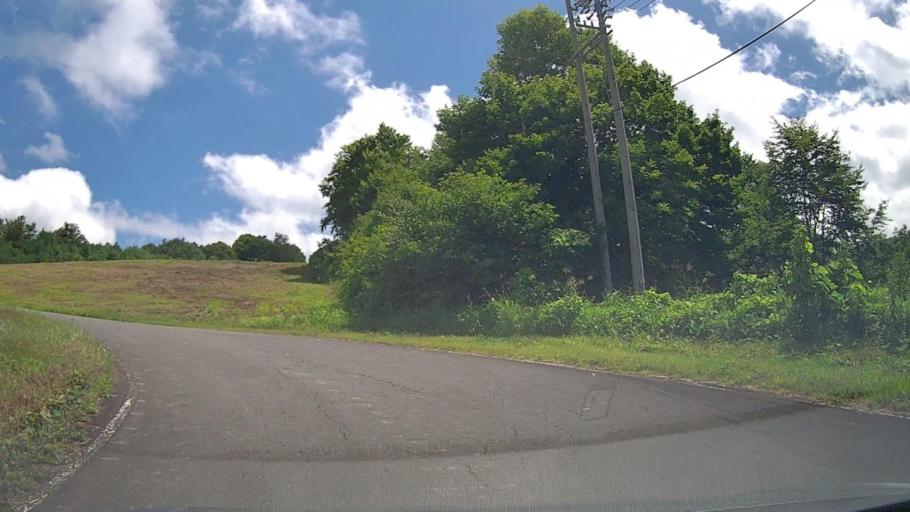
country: JP
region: Nagano
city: Iiyama
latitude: 36.9256
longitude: 138.4682
